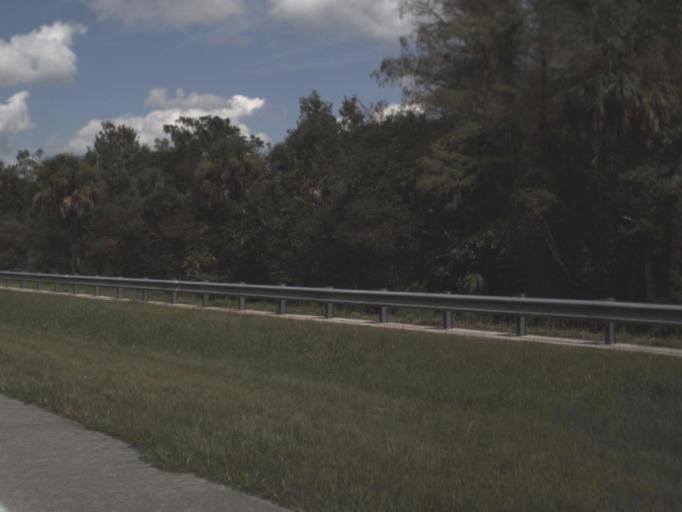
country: US
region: Florida
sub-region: Collier County
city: Orangetree
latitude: 26.0829
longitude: -81.3447
